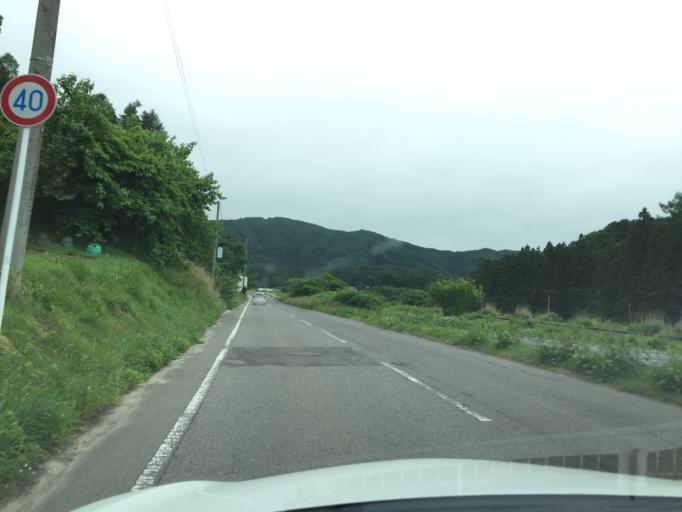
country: JP
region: Fukushima
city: Funehikimachi-funehiki
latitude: 37.3599
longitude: 140.6388
